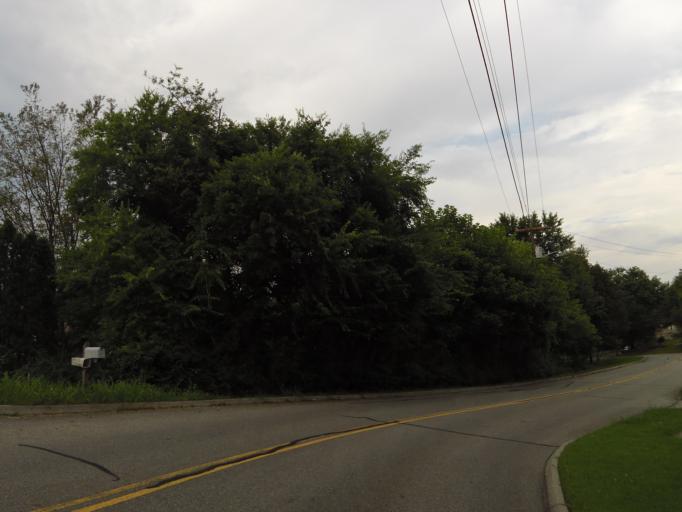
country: US
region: Tennessee
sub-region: Blount County
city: Maryville
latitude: 35.7467
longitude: -83.9932
